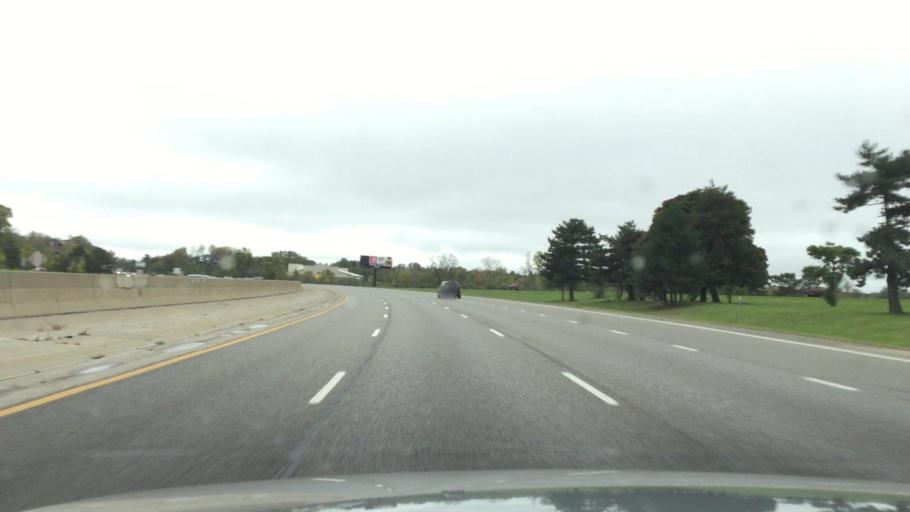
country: US
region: Michigan
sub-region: Genesee County
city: Beecher
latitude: 43.0605
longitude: -83.7626
